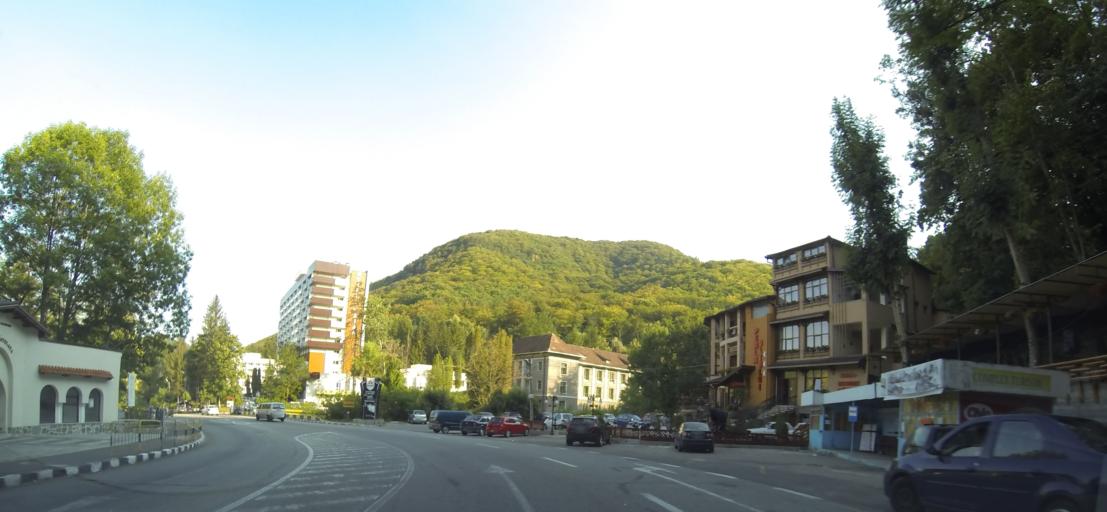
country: RO
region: Valcea
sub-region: Oras Calimanesti
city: Calimanesti
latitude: 45.2603
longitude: 24.3194
